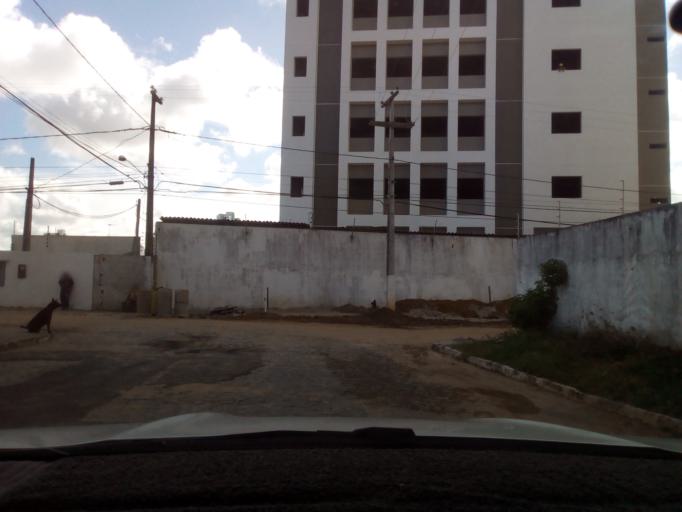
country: BR
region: Paraiba
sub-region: Joao Pessoa
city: Joao Pessoa
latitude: -7.1079
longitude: -34.8423
